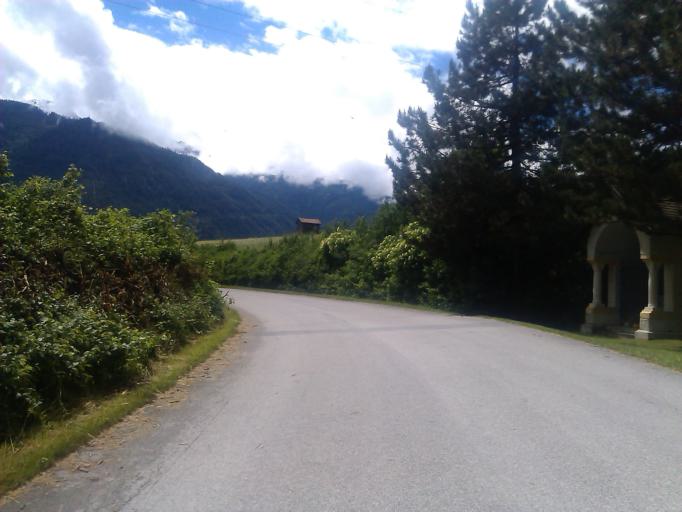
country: AT
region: Tyrol
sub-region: Politischer Bezirk Landeck
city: Prutz
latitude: 47.0930
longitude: 10.6608
